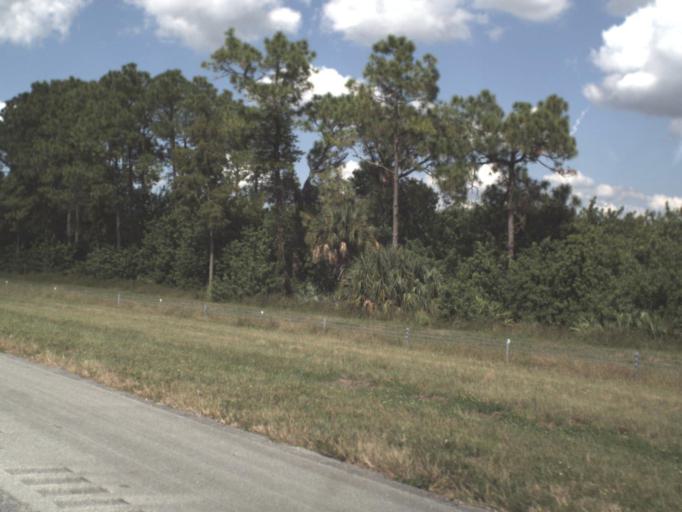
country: US
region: Florida
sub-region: Indian River County
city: West Vero Corridor
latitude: 27.5312
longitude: -80.6065
